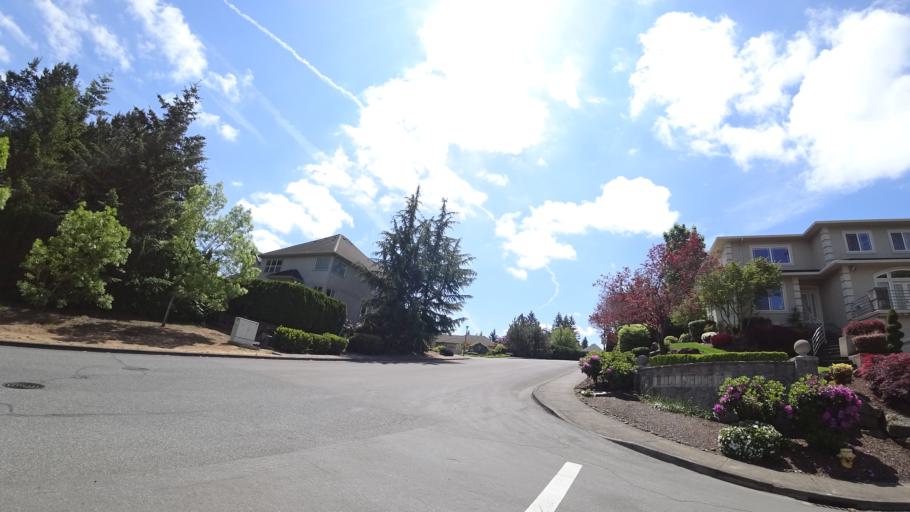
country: US
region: Oregon
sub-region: Washington County
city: King City
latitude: 45.4254
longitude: -122.8161
